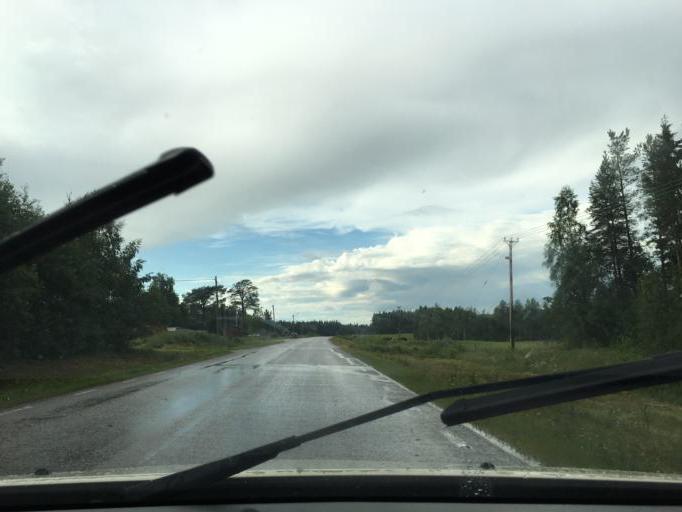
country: SE
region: Norrbotten
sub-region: Kalix Kommun
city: Toere
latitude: 65.9664
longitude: 22.8735
